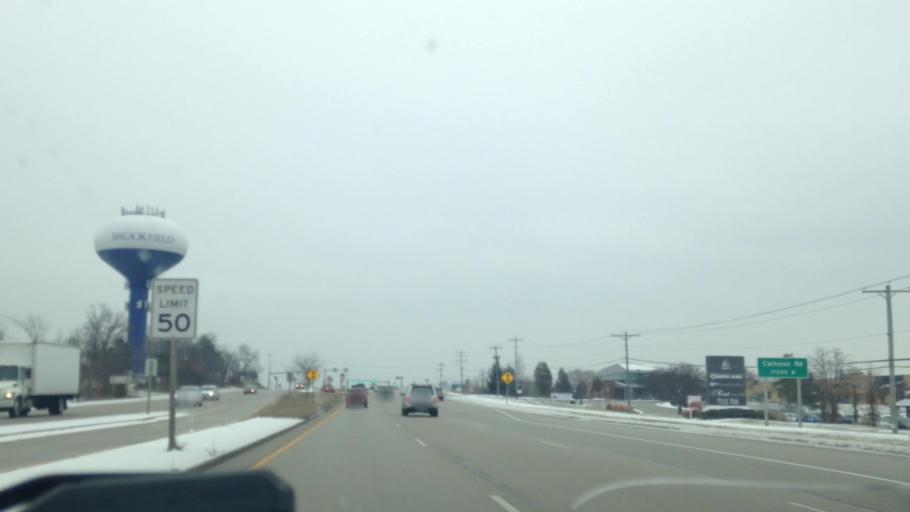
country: US
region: Wisconsin
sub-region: Waukesha County
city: Brookfield
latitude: 43.0901
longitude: -88.1304
